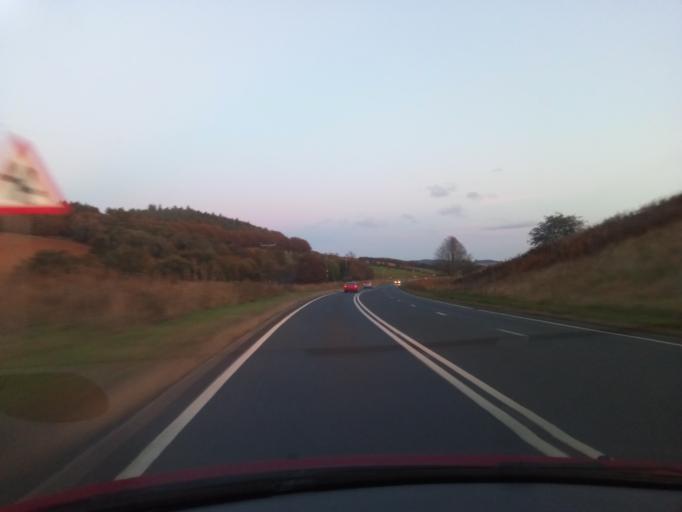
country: GB
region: Scotland
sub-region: The Scottish Borders
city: Lauder
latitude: 55.7833
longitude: -2.8129
